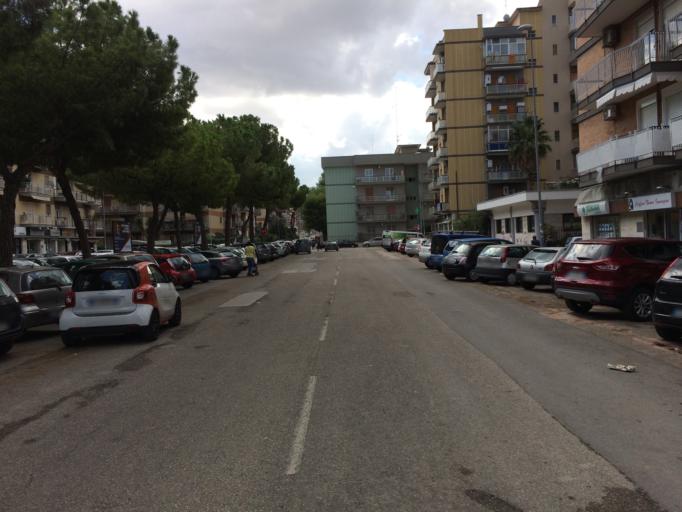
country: IT
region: Apulia
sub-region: Provincia di Bari
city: Bari
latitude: 41.1037
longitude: 16.8774
